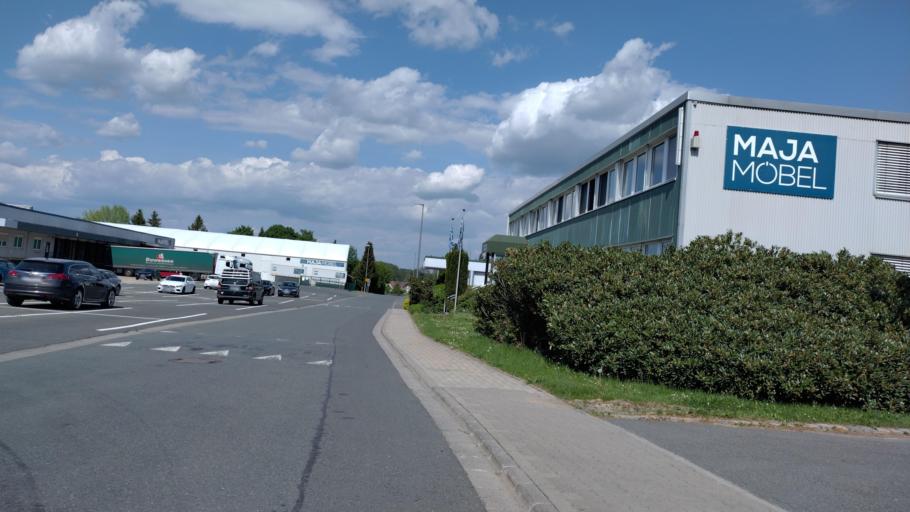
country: DE
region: Bavaria
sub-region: Upper Franconia
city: Kasendorf
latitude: 50.0396
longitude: 11.3600
